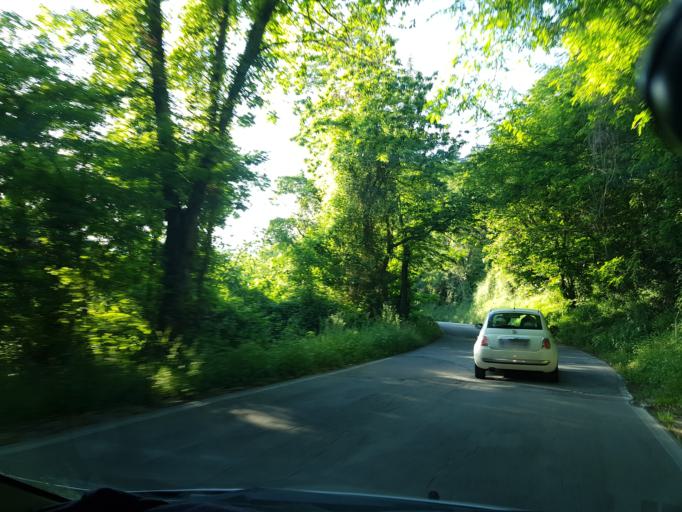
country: IT
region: Tuscany
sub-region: Provincia di Lucca
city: Minucciano
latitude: 44.1848
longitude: 10.1957
